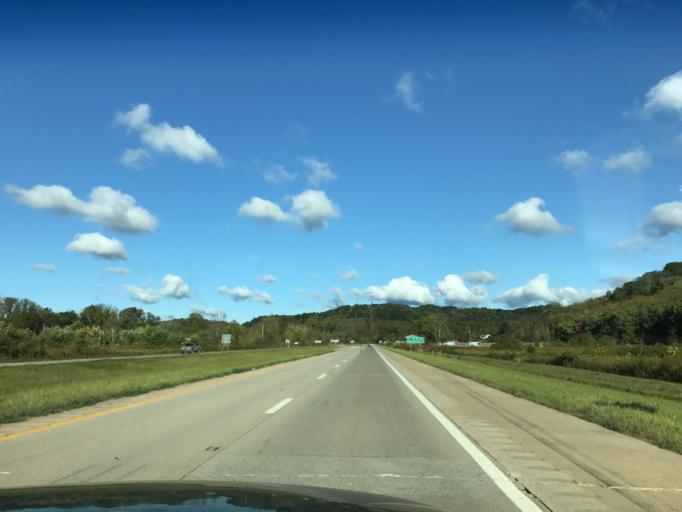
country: US
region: Ohio
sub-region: Athens County
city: Athens
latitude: 39.3279
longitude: -82.0000
